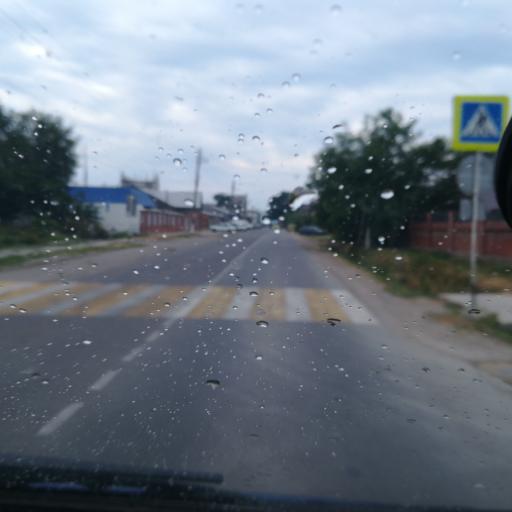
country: RU
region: Krasnodarskiy
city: Krymsk
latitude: 44.9350
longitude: 37.9809
